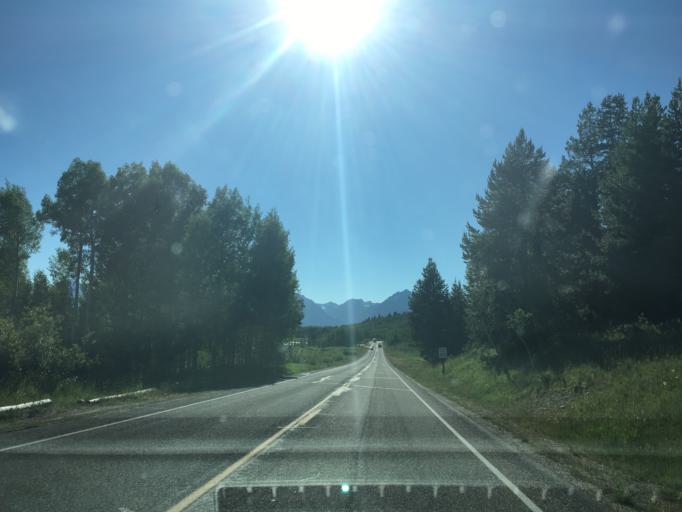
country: US
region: Wyoming
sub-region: Teton County
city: Jackson
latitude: 43.8656
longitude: -110.5421
